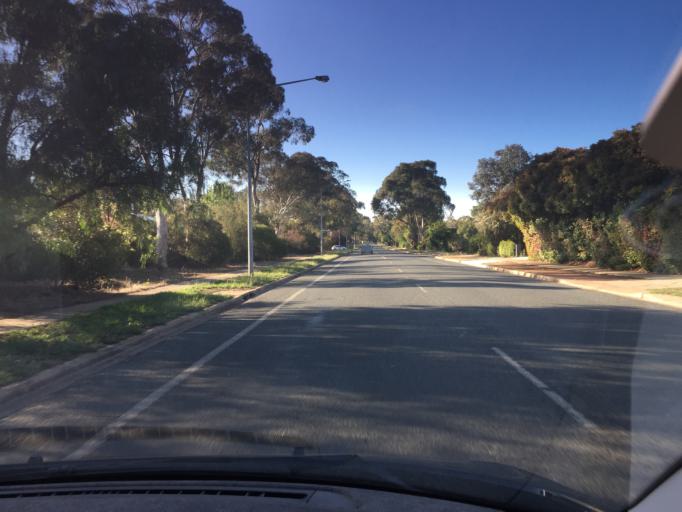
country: AU
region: Australian Capital Territory
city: Kaleen
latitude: -35.2251
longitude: 149.1111
